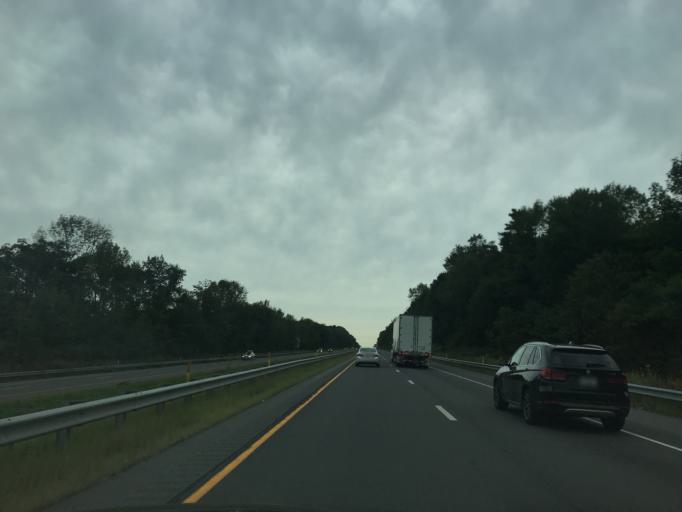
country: US
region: Pennsylvania
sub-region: Susquehanna County
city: Susquehanna
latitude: 41.8322
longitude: -75.6804
